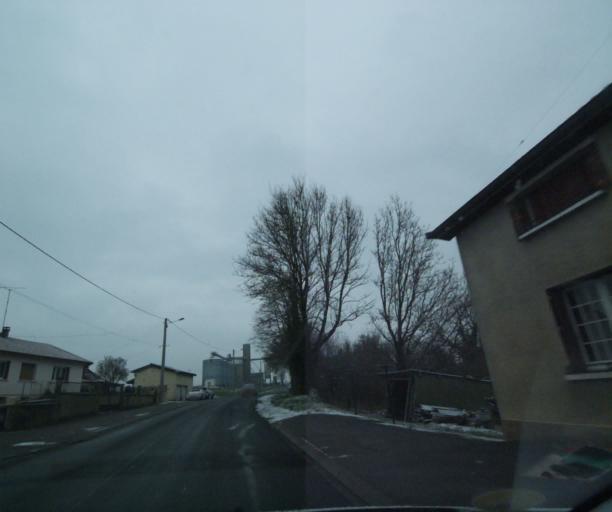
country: FR
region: Champagne-Ardenne
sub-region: Departement de la Haute-Marne
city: Wassy
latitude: 48.4366
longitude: 4.9606
